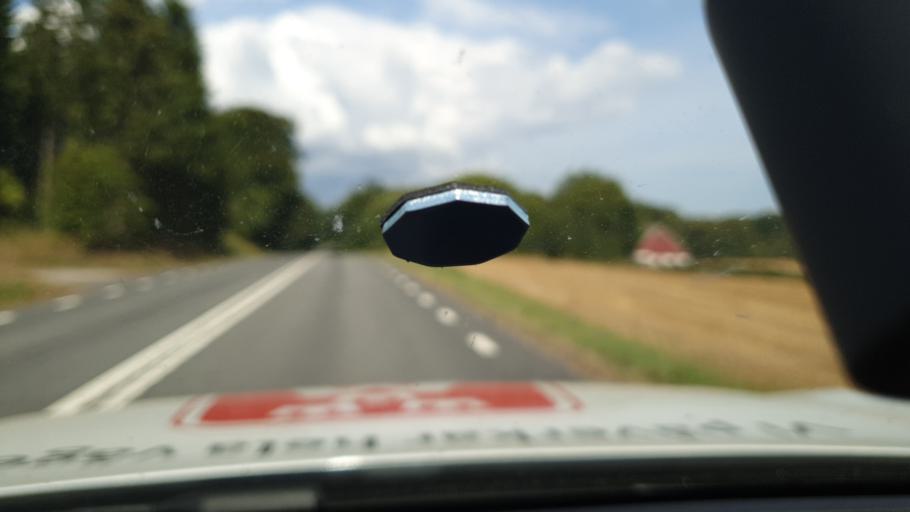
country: SE
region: Skane
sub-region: Simrishamns Kommun
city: Kivik
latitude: 55.6286
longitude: 14.1345
